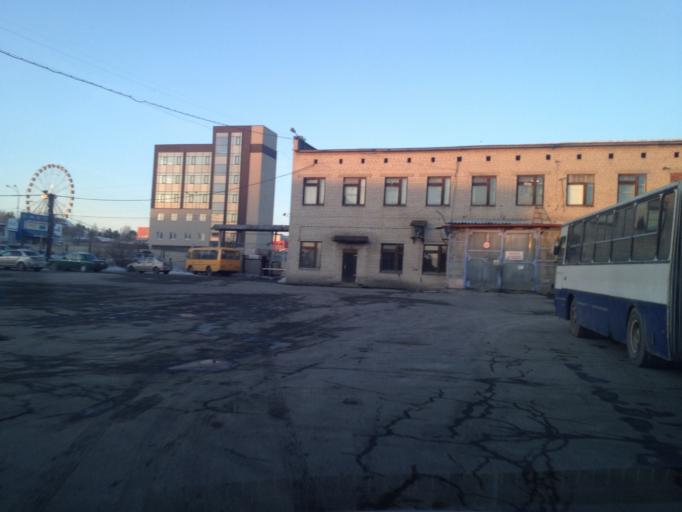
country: RU
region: Sverdlovsk
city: Sovkhoznyy
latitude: 56.8110
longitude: 60.5415
